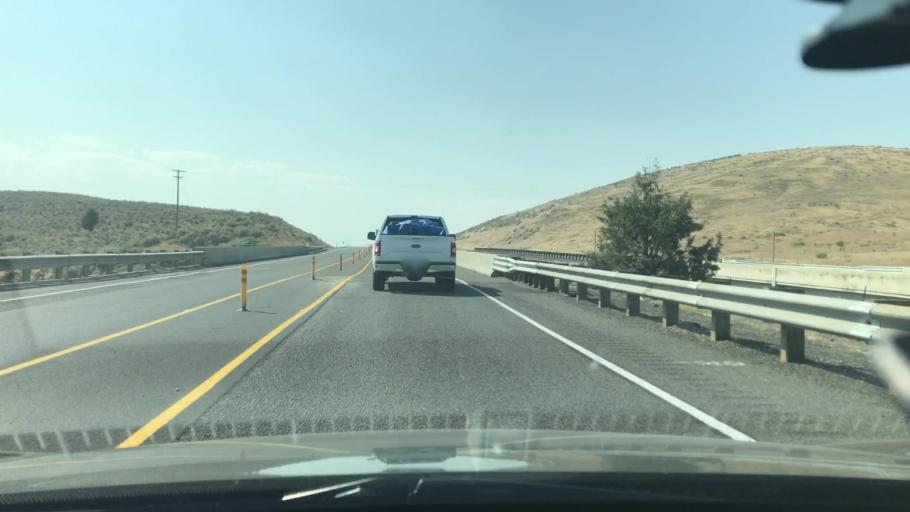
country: US
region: Oregon
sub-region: Baker County
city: Baker City
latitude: 44.6826
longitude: -117.6590
